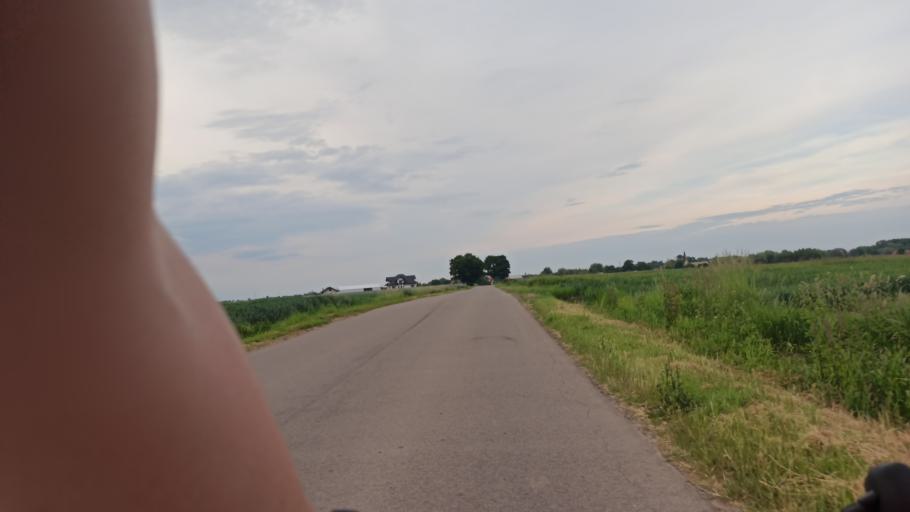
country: PL
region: Subcarpathian Voivodeship
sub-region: Powiat jaroslawski
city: Radymno
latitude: 49.9267
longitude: 22.8043
